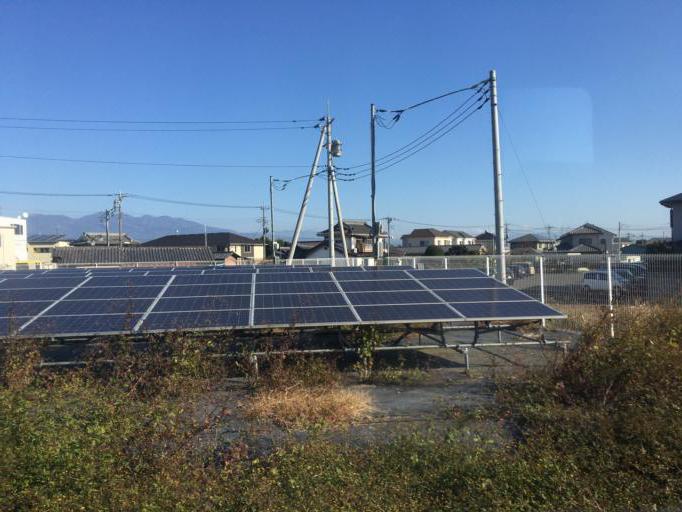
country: JP
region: Gunma
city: Maebashi-shi
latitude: 36.3674
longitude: 139.1153
